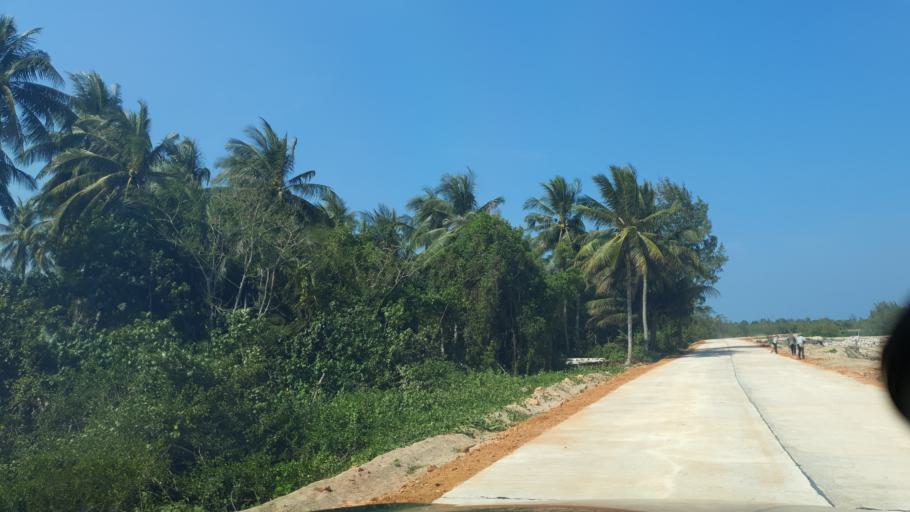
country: TH
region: Surat Thani
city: Tha Chana
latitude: 9.5897
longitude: 99.2077
